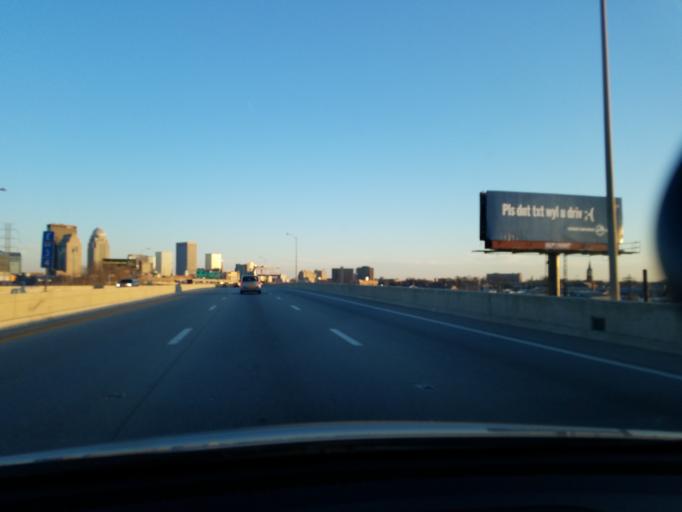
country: US
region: Kentucky
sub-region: Jefferson County
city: Louisville
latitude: 38.2631
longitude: -85.7727
